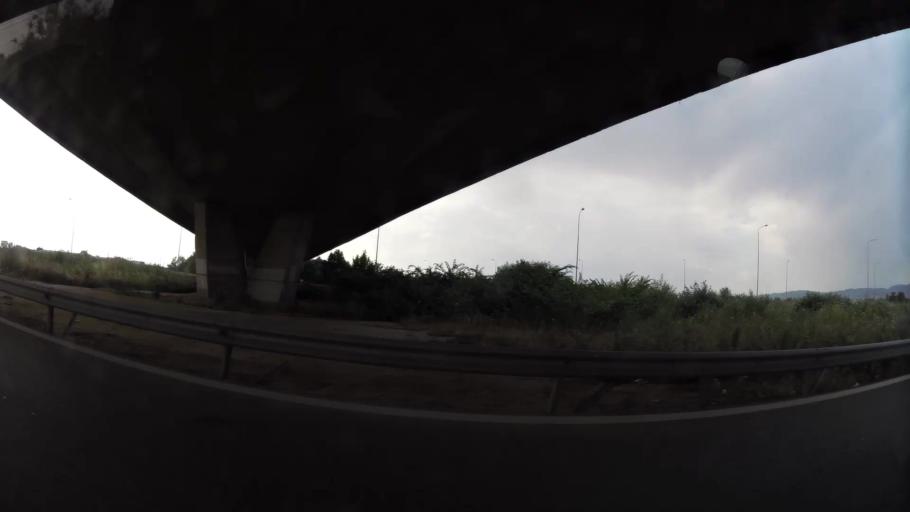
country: GR
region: Central Macedonia
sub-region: Nomos Thessalonikis
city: Sindos
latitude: 40.6493
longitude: 22.8128
